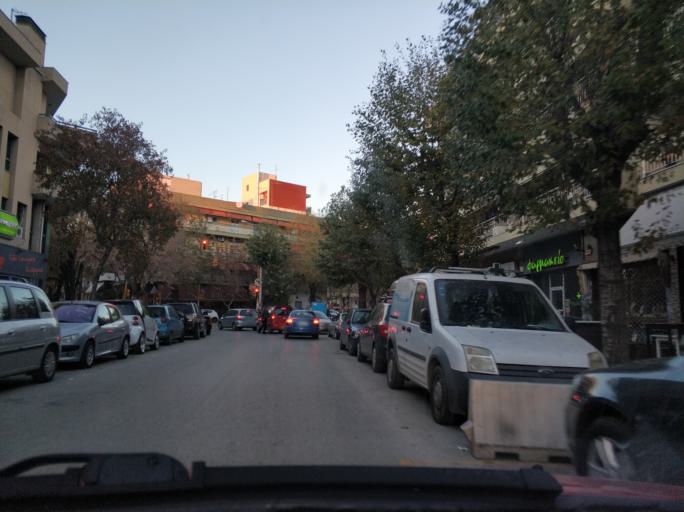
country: GR
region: Central Macedonia
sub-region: Nomos Thessalonikis
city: Pylaia
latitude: 40.5992
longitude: 22.9727
